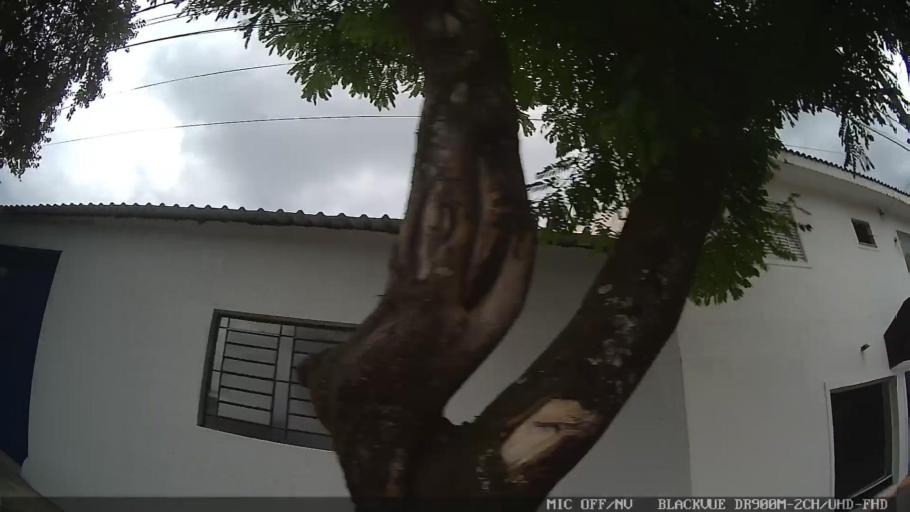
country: BR
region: Sao Paulo
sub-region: Amparo
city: Amparo
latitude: -22.6990
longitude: -46.7596
